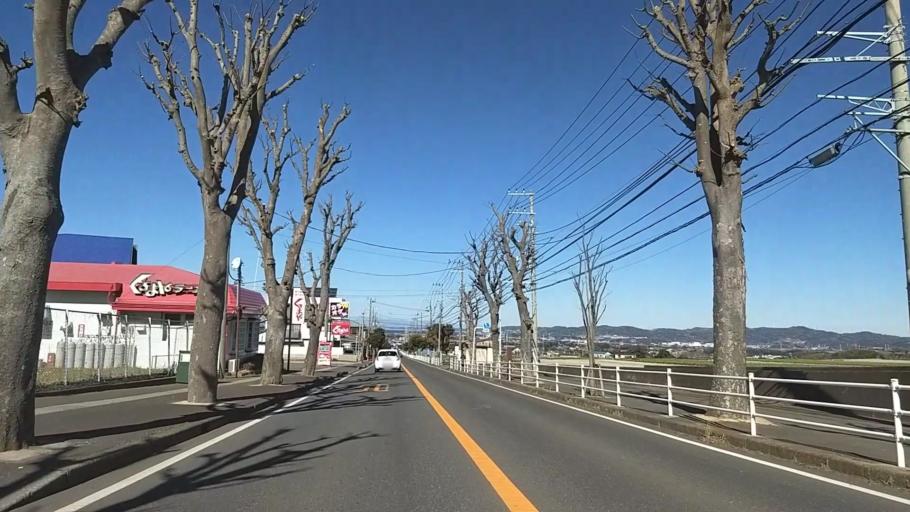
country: JP
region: Kanagawa
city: Miura
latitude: 35.1696
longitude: 139.6391
